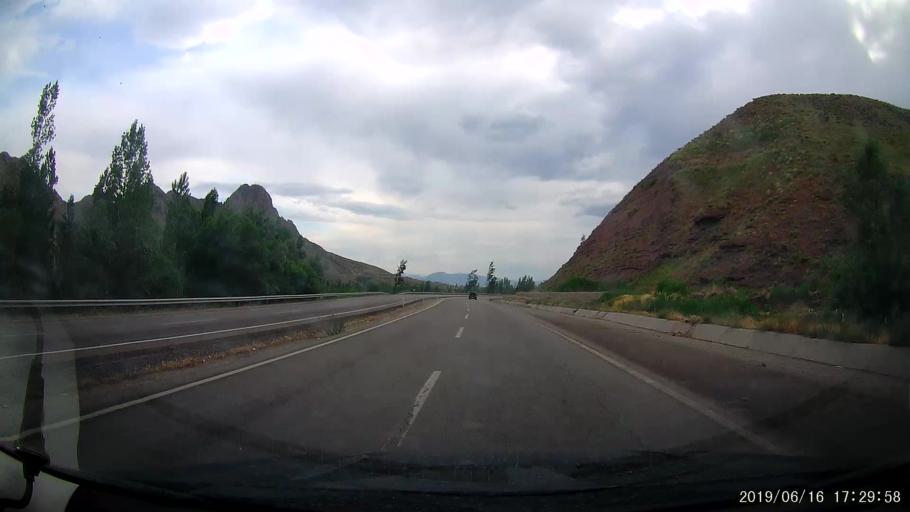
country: TR
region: Erzincan
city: Tercan
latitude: 39.7793
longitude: 40.3560
